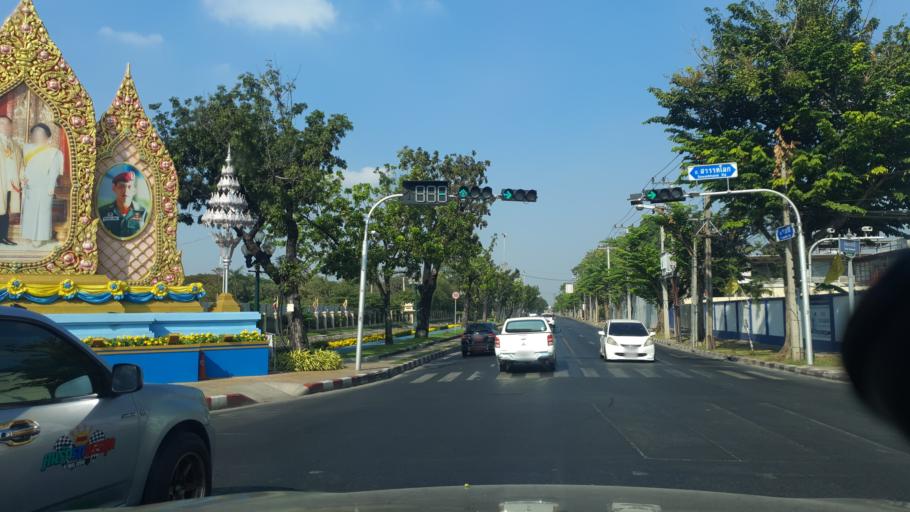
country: TH
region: Bangkok
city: Dusit
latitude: 13.7705
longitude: 100.5260
